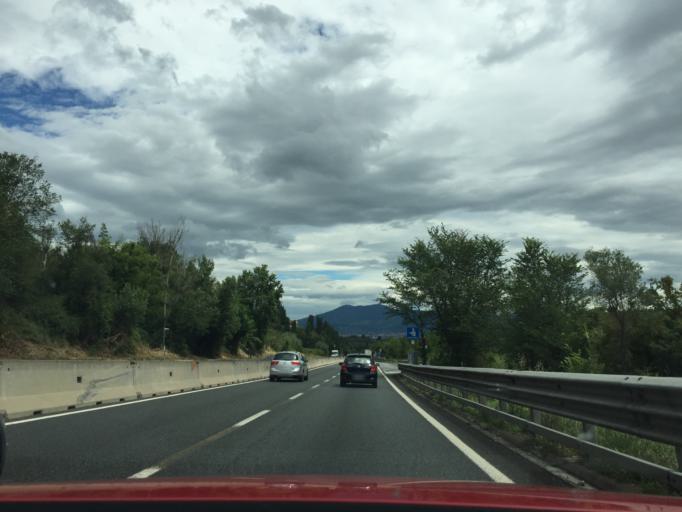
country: IT
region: Tuscany
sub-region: Province of Florence
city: Lastra a Signa
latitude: 43.7480
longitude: 11.1215
